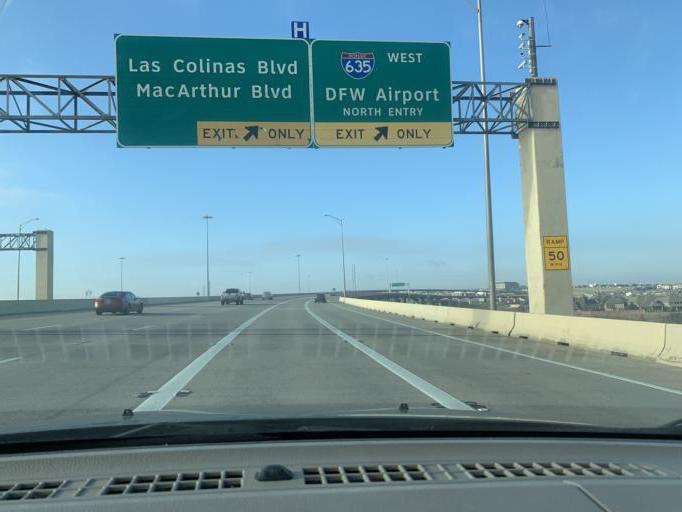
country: US
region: Texas
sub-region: Dallas County
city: Farmers Branch
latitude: 32.9150
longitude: -96.9374
